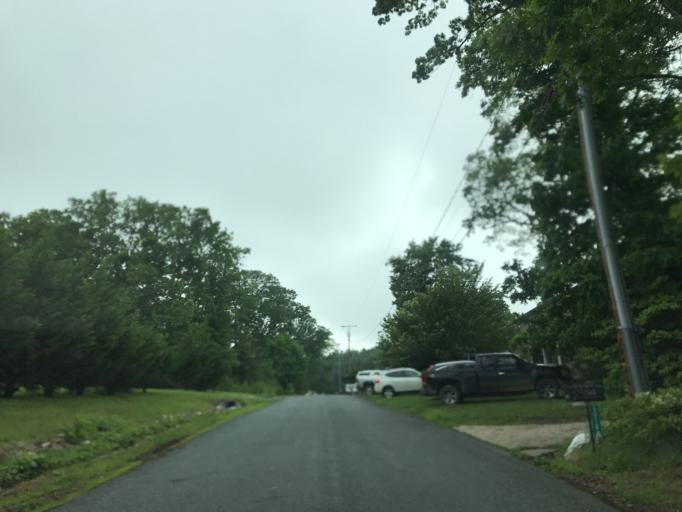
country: US
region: Maryland
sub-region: Harford County
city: Jarrettsville
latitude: 39.7030
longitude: -76.4865
